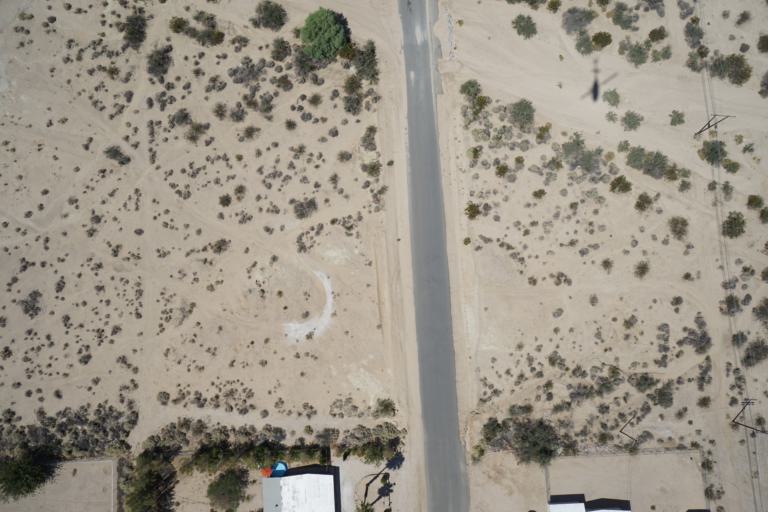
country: US
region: California
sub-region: San Bernardino County
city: Twentynine Palms
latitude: 34.1347
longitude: -116.0397
